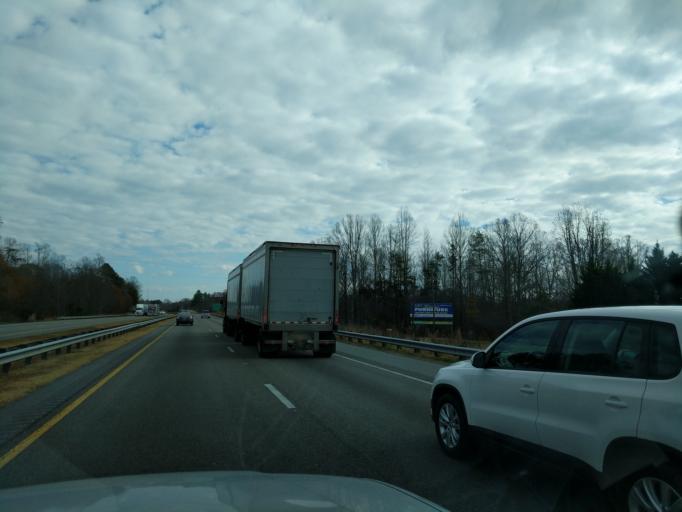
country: US
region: North Carolina
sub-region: Burke County
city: Hildebran
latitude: 35.7084
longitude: -81.4356
